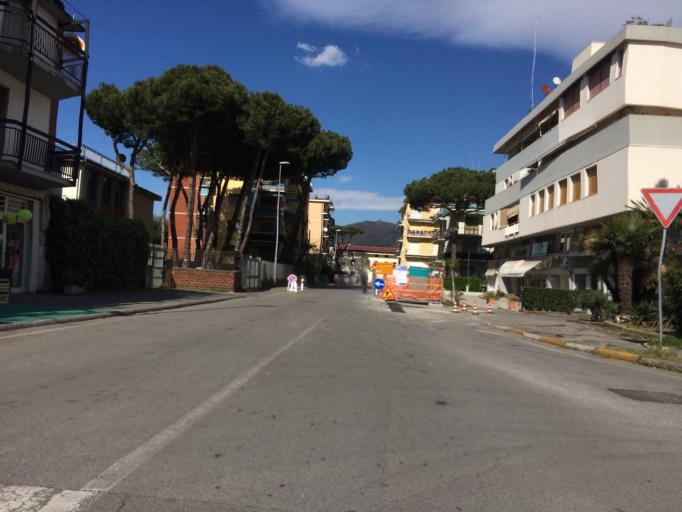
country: IT
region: Tuscany
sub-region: Provincia di Massa-Carrara
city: Marina di Carrara
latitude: 44.0425
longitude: 10.0353
